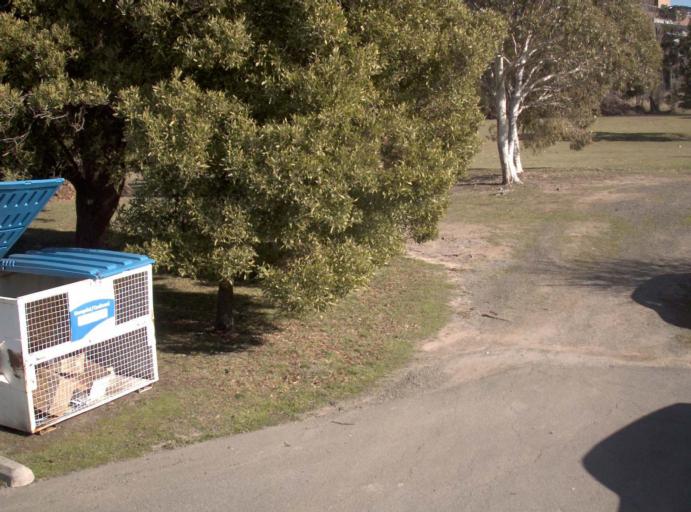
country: AU
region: Tasmania
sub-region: Launceston
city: Summerhill
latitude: -41.4733
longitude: 147.1583
